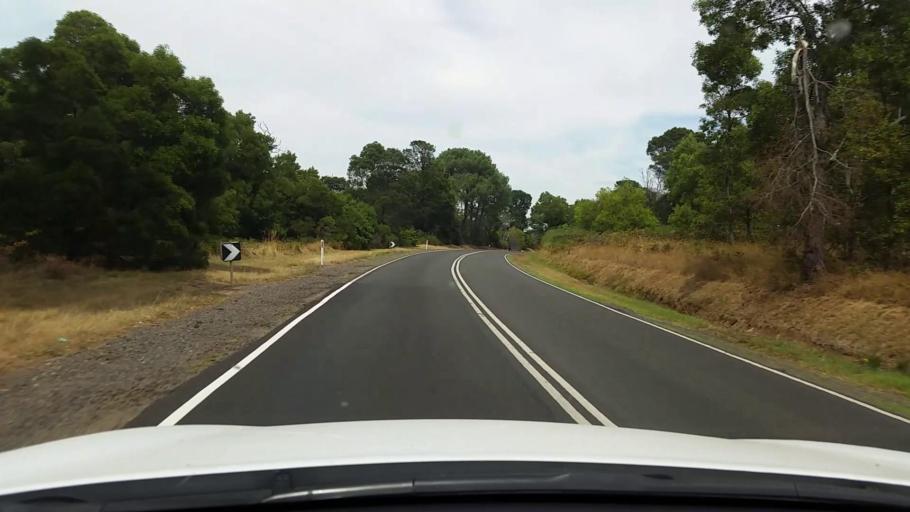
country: AU
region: Victoria
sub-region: Mornington Peninsula
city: Merricks
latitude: -38.3821
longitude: 145.1091
